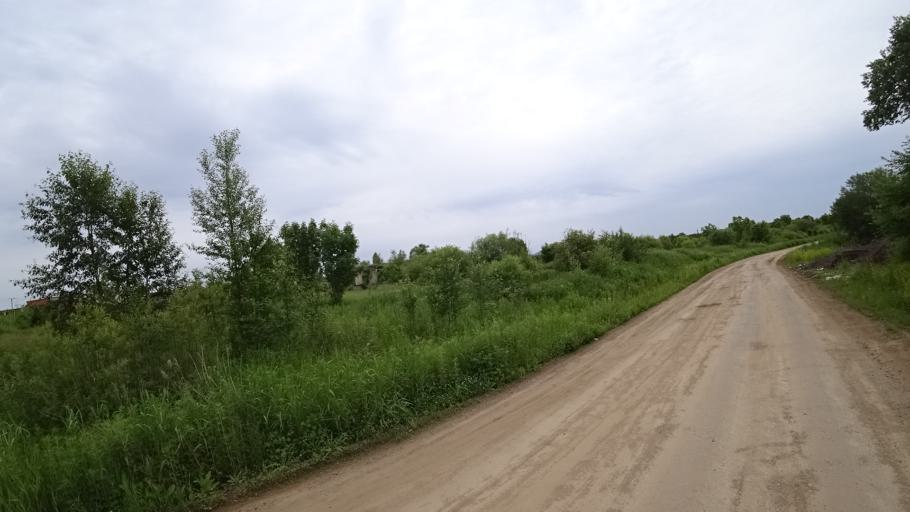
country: RU
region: Primorskiy
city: Arsen'yev
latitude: 44.1990
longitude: 133.3095
